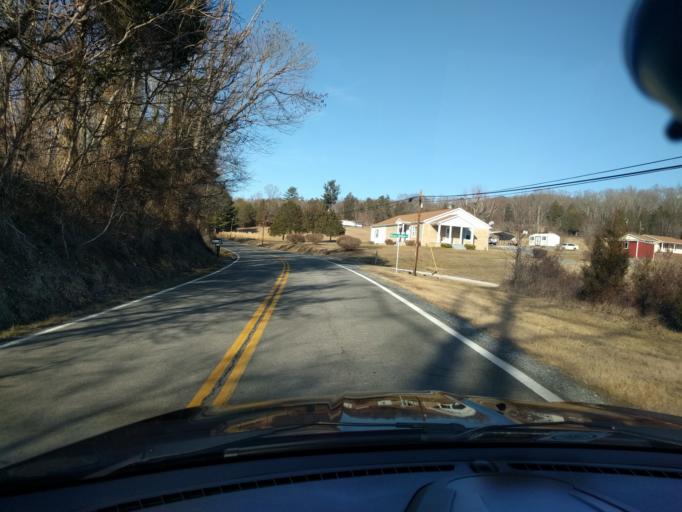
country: US
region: Virginia
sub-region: Botetourt County
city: Buchanan
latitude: 37.5550
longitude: -79.7252
